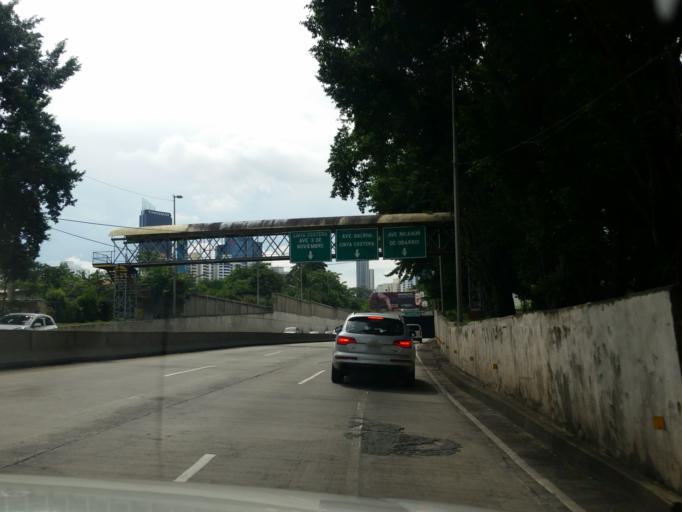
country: PA
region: Panama
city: Panama
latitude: 8.9792
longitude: -79.5127
